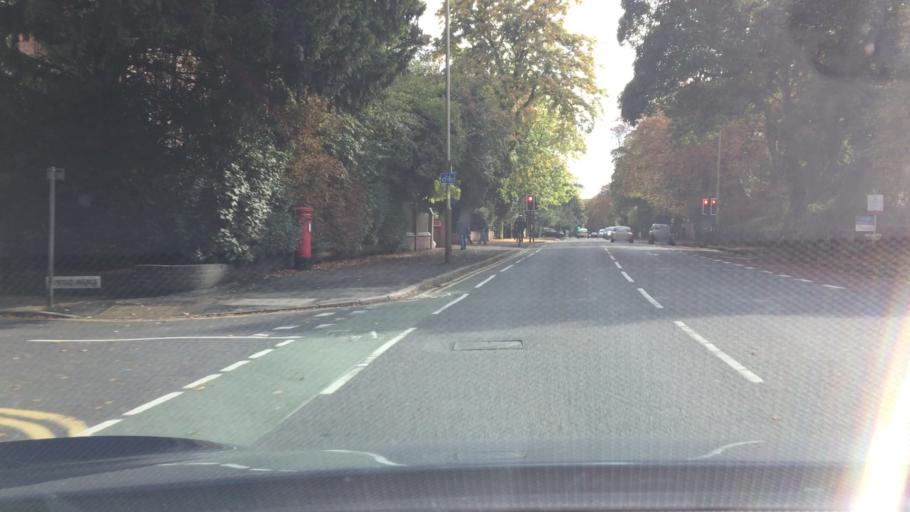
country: GB
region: England
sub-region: City of Leicester
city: Leicester
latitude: 52.6219
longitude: -1.1128
